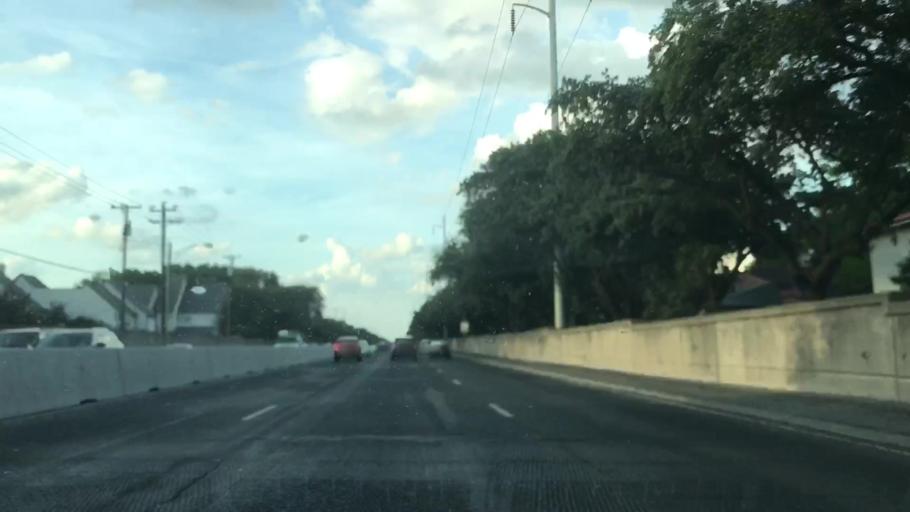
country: US
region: Texas
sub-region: Dallas County
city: Highland Park
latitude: 32.8232
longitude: -96.8166
